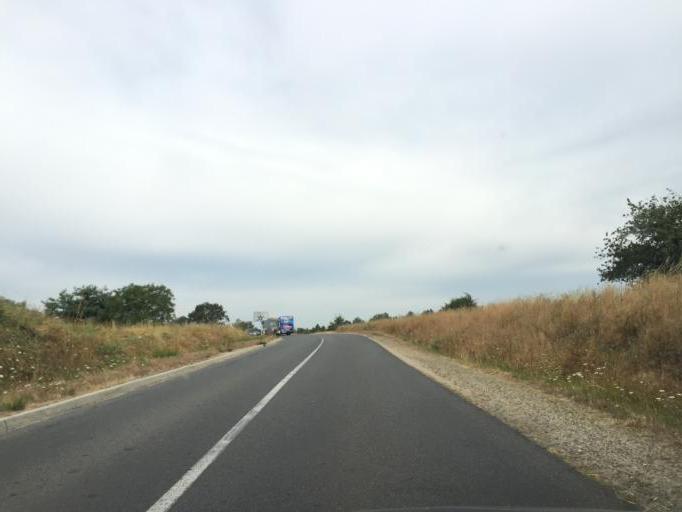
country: FR
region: Auvergne
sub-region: Departement de l'Allier
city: Moulins
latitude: 46.5877
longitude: 3.3366
